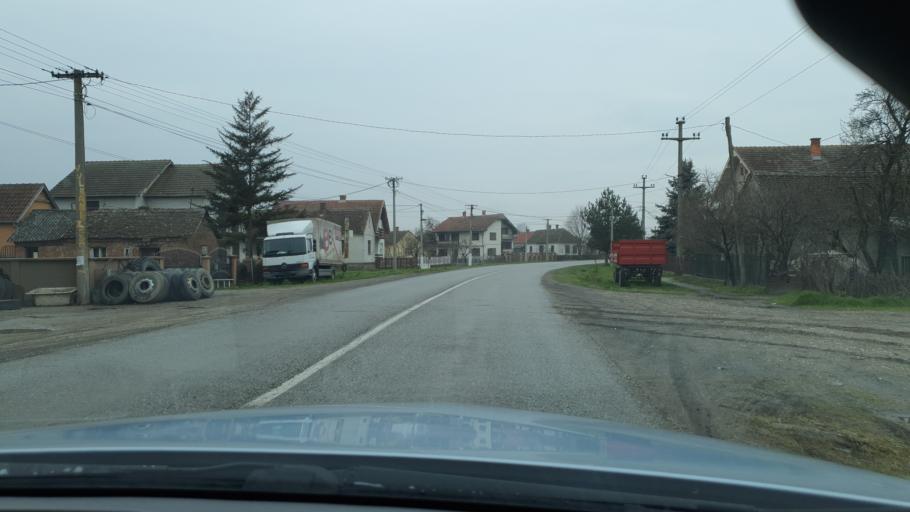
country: RS
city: Stitar
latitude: 44.7824
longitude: 19.5999
